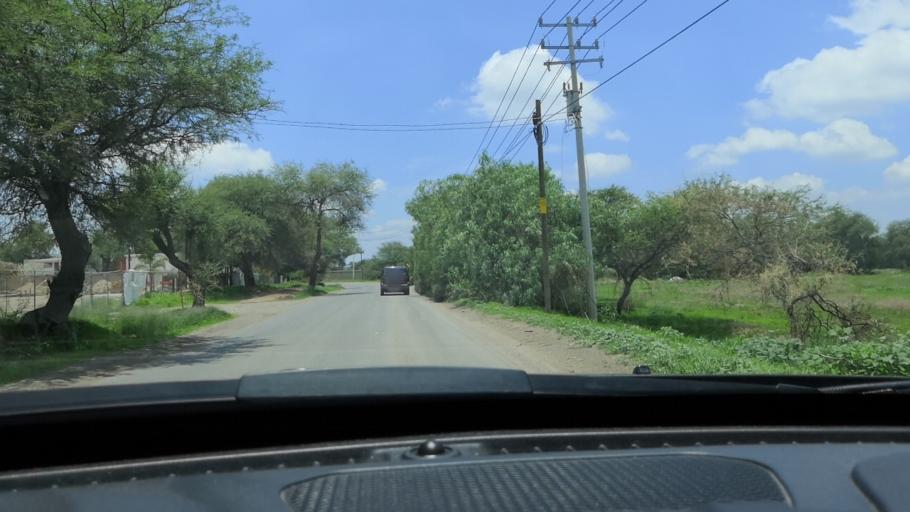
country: MX
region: Guanajuato
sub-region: Leon
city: Ladrilleras del Refugio
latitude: 21.0524
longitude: -101.5627
